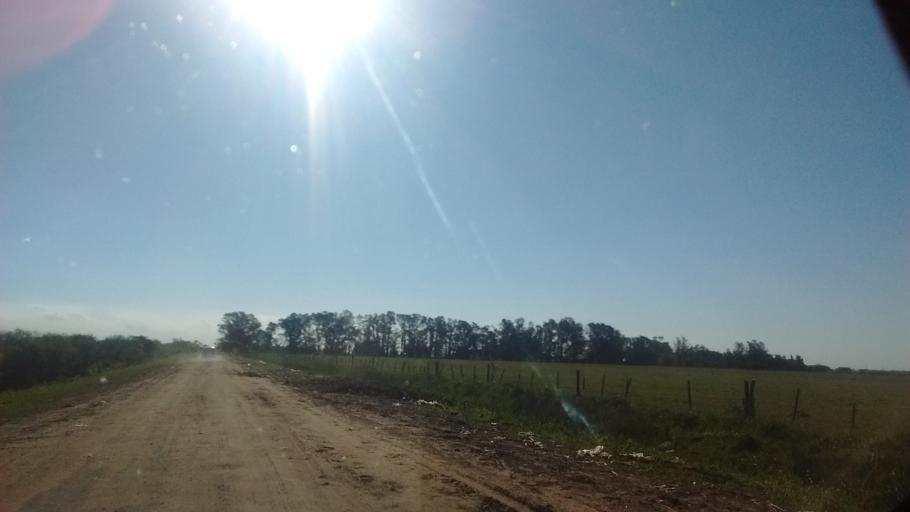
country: AR
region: Santa Fe
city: Funes
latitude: -32.8935
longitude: -60.7987
